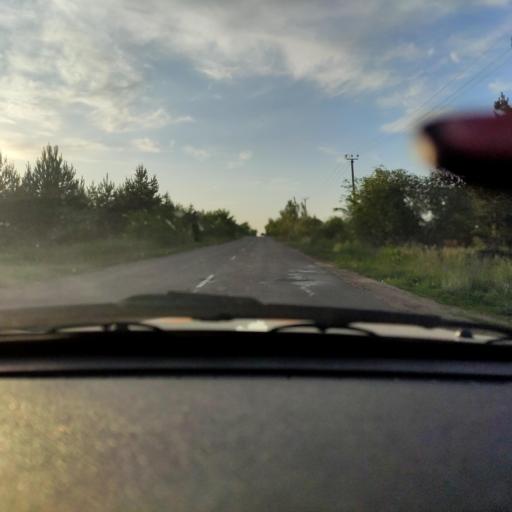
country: RU
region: Voronezj
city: Podgornoye
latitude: 51.8316
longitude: 39.2053
